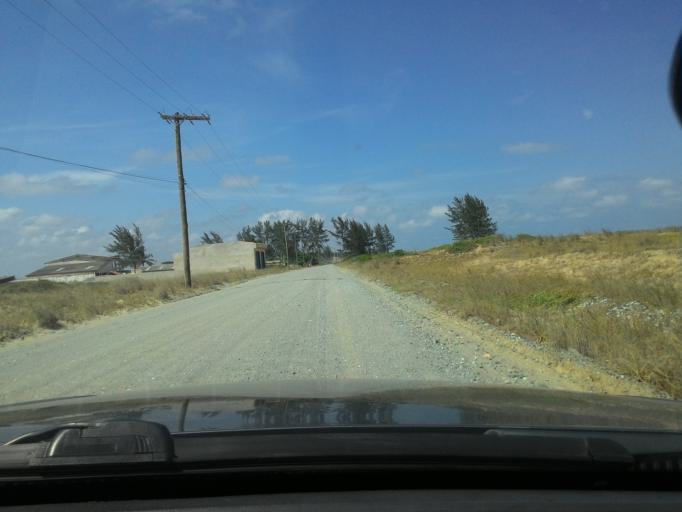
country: BR
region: Sao Paulo
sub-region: Iguape
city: Iguape
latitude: -24.8380
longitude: -47.6783
